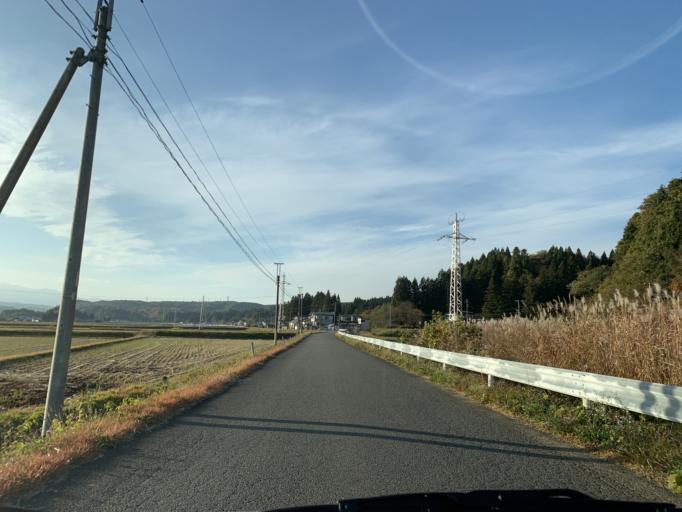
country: JP
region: Iwate
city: Ichinoseki
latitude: 38.9466
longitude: 141.0610
